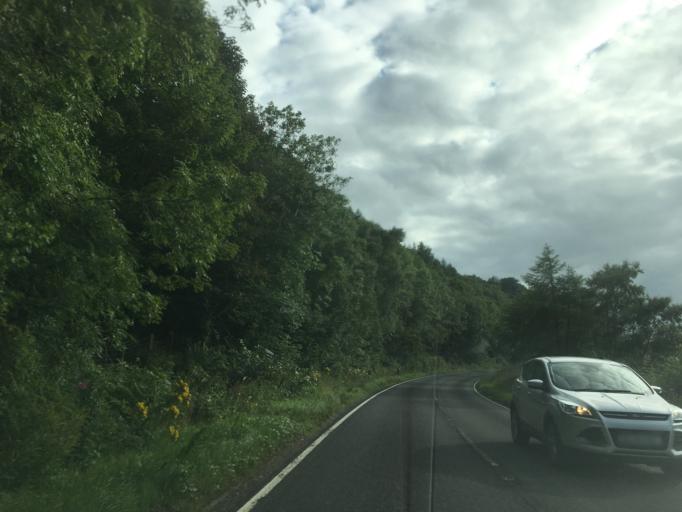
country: GB
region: Scotland
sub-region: Argyll and Bute
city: Oban
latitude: 56.3559
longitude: -5.4641
